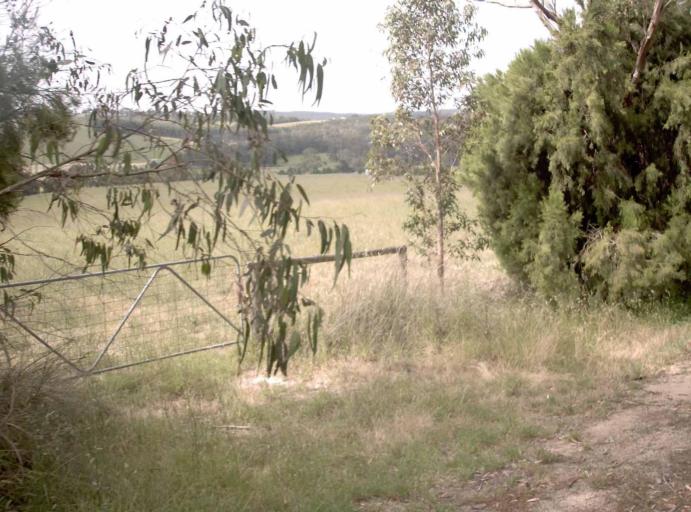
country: AU
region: Victoria
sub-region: Latrobe
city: Traralgon
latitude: -38.3800
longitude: 146.7710
